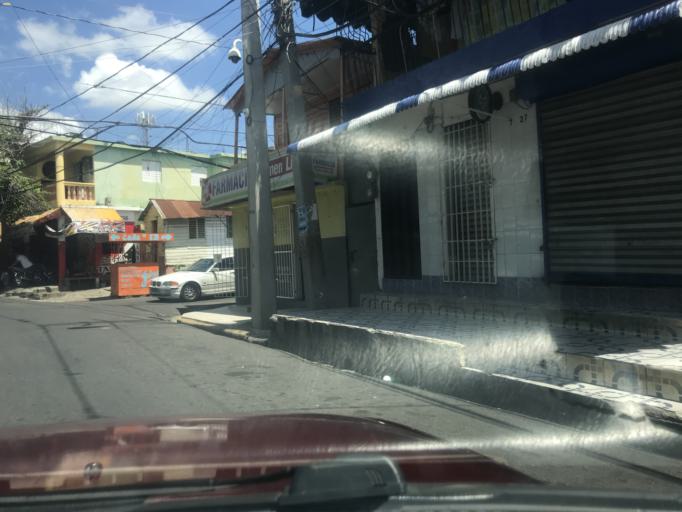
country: DO
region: Santiago
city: Santiago de los Caballeros
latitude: 19.4674
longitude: -70.6998
